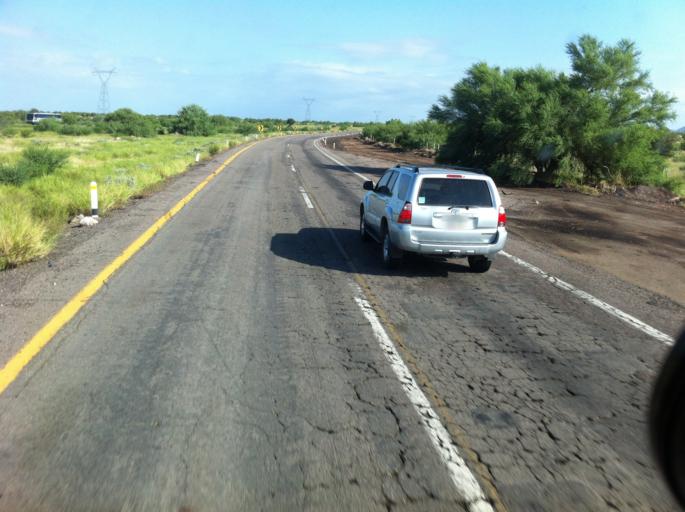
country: MX
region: Sonora
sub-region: Hermosillo
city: Miguel Aleman (La Doce)
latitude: 28.5241
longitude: -111.0468
